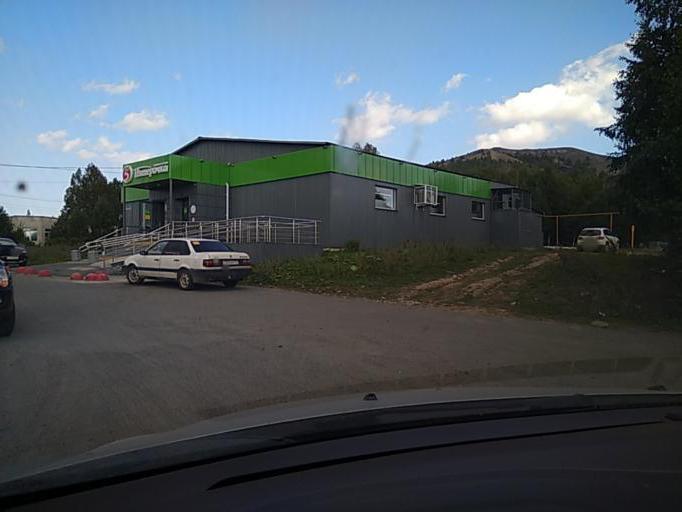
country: RU
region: Chelyabinsk
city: Karabash
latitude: 55.4886
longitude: 60.2394
